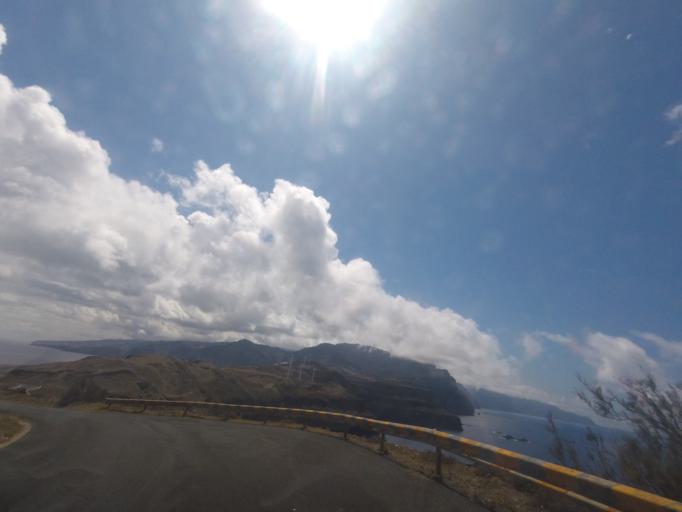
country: PT
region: Madeira
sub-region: Machico
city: Canical
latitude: 32.7488
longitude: -16.7128
